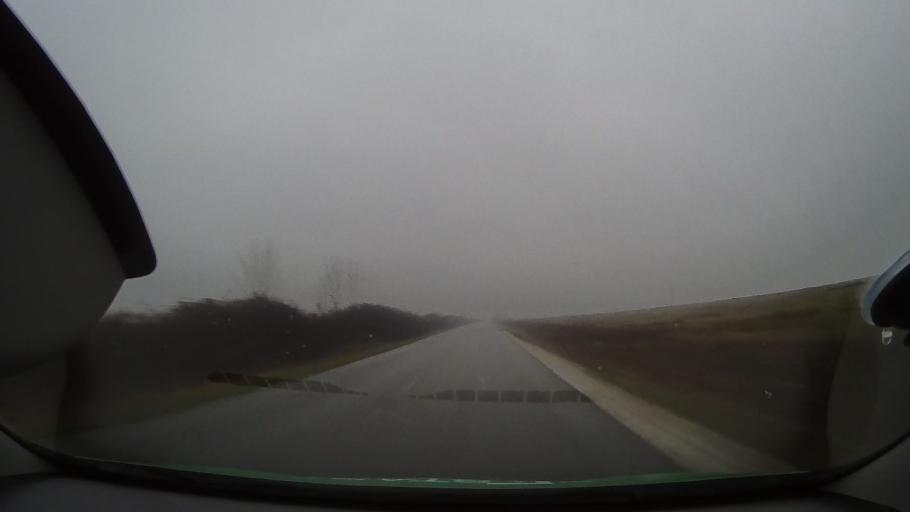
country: RO
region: Arad
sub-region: Comuna Craiova
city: Craiova
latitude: 46.6101
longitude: 21.9570
